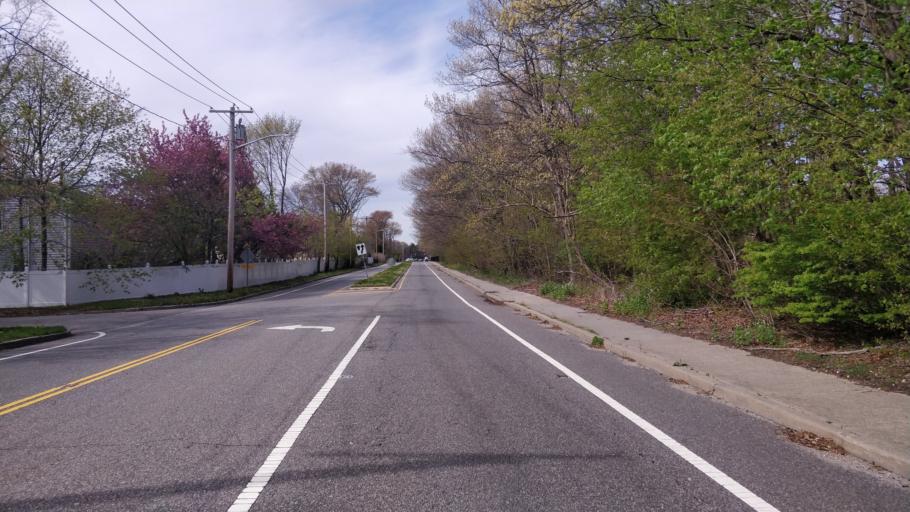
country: US
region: New York
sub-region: Suffolk County
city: Terryville
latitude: 40.8934
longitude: -73.0795
